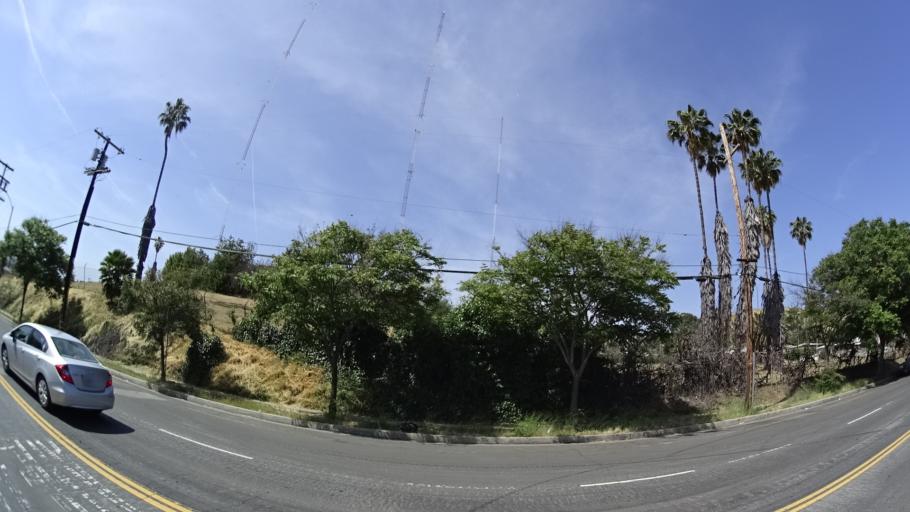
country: US
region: California
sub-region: Los Angeles County
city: Boyle Heights
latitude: 34.0689
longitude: -118.1936
